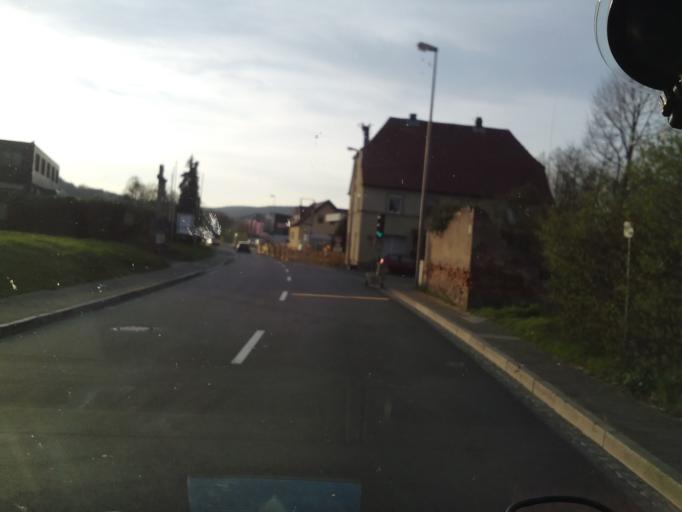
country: DE
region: Bavaria
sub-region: Upper Franconia
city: Baunach
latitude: 49.9896
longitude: 10.8464
